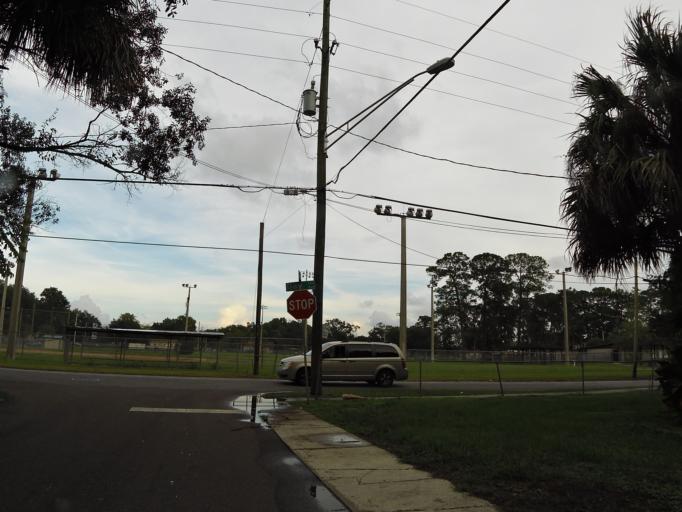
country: US
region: Florida
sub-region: Duval County
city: Jacksonville
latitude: 30.3235
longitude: -81.7099
